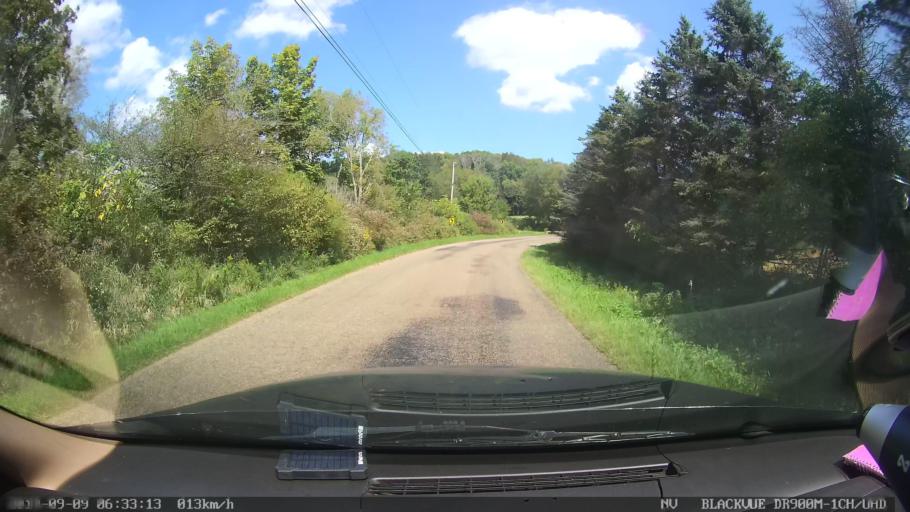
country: US
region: Ohio
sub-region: Sandusky County
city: Bellville
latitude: 40.6519
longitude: -82.4817
